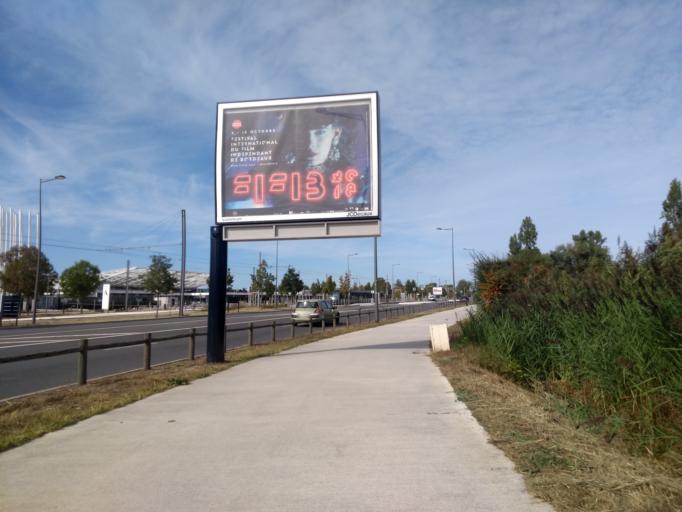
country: FR
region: Aquitaine
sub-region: Departement de la Gironde
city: Le Bouscat
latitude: 44.8922
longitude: -0.5653
